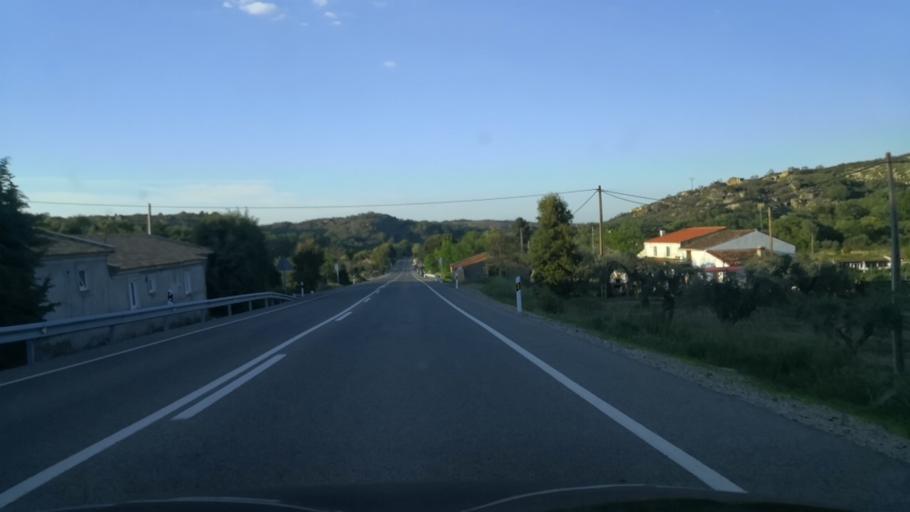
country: PT
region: Portalegre
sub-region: Portalegre
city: Sao Juliao
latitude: 39.3601
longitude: -7.2745
